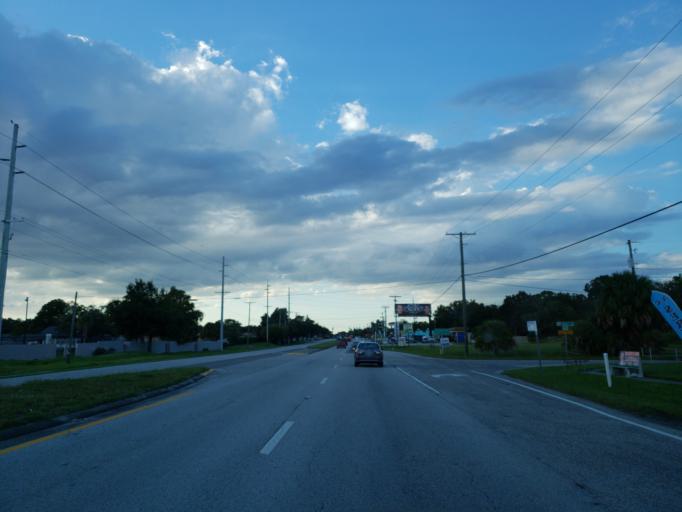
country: US
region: Florida
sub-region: Hillsborough County
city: Carrollwood Village
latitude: 28.0456
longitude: -82.5153
